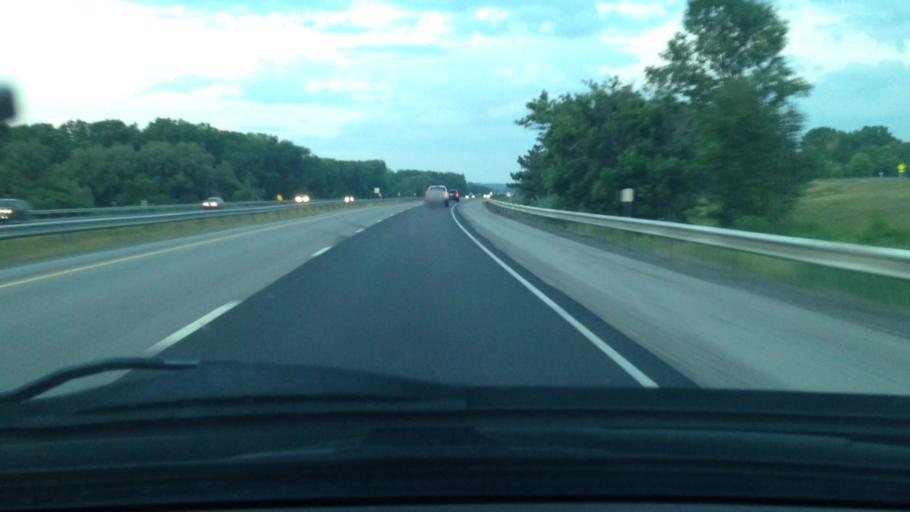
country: US
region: New York
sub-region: Montgomery County
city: Fonda
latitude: 42.9098
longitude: -74.4536
